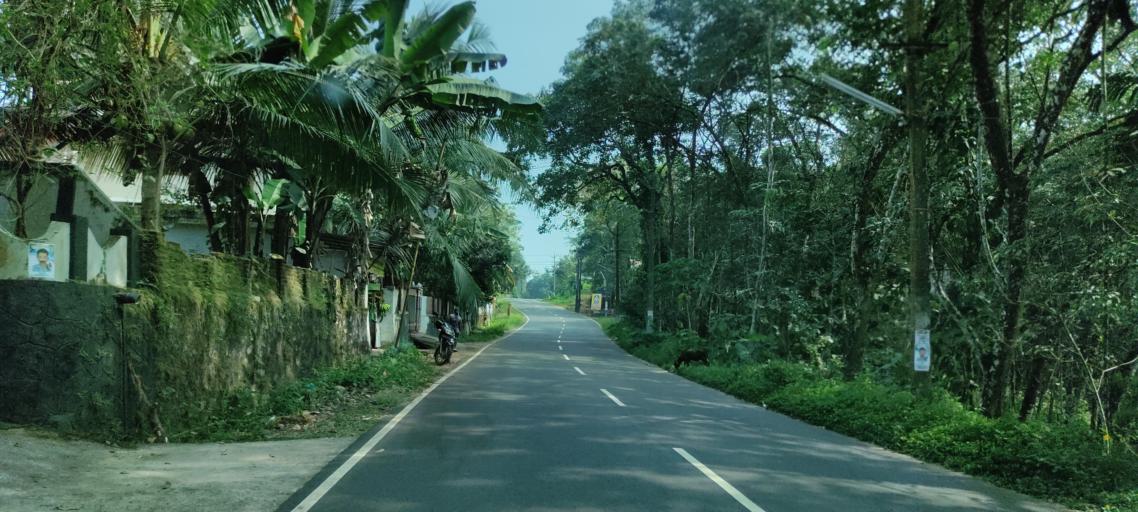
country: IN
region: Kerala
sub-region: Pattanamtitta
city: Adur
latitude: 9.2367
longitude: 76.6860
